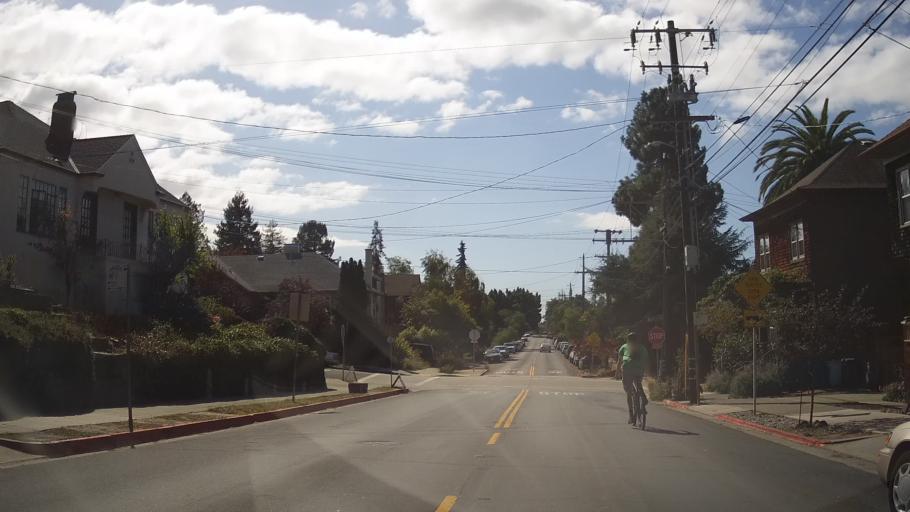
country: US
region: California
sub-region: Alameda County
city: Berkeley
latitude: 37.8829
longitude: -122.2662
